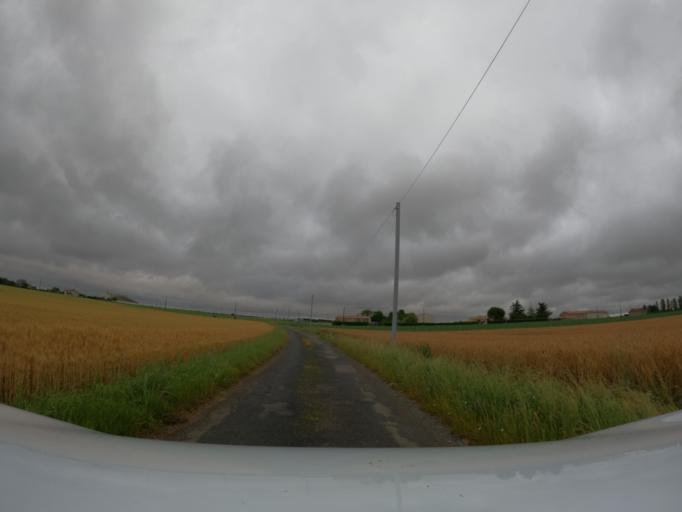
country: FR
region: Pays de la Loire
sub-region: Departement de la Vendee
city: Maillezais
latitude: 46.4041
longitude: -0.7384
